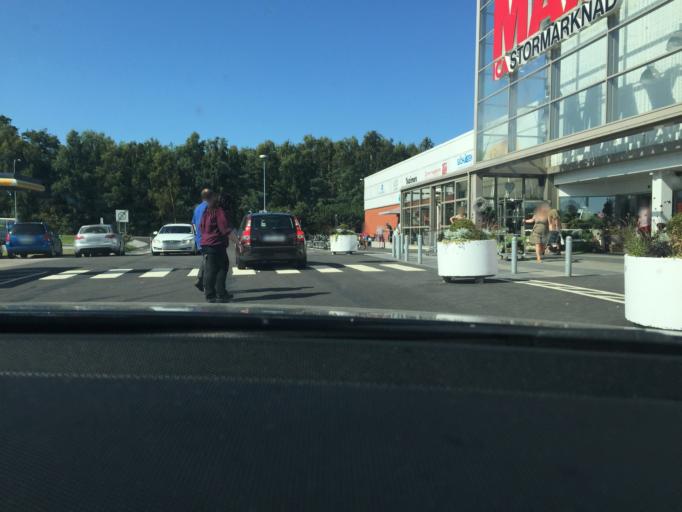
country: SE
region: Halland
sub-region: Laholms Kommun
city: Mellbystrand
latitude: 56.5027
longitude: 12.9571
